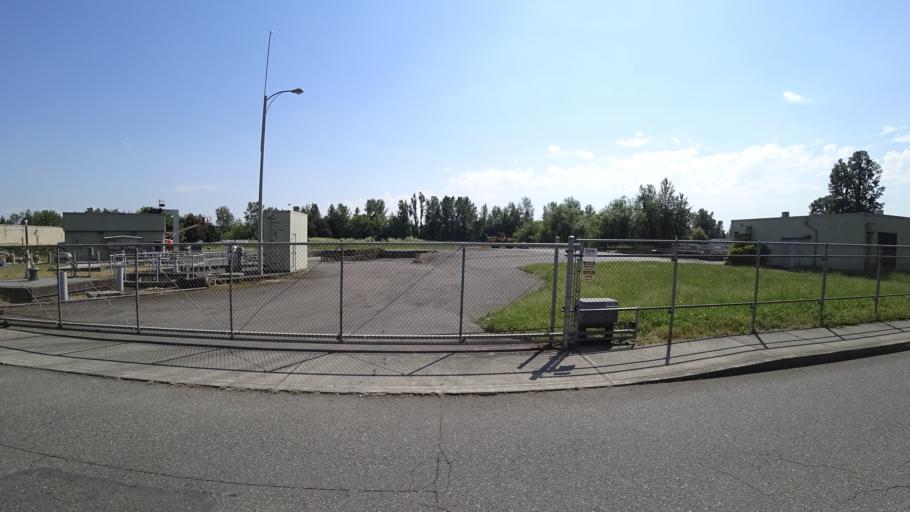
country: US
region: Oregon
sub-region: Multnomah County
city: Lents
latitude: 45.5640
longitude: -122.5400
